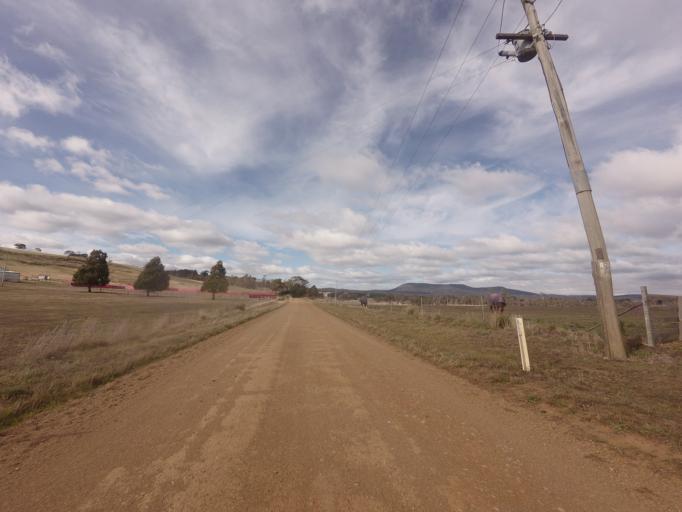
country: AU
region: Tasmania
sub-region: Sorell
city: Sorell
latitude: -42.4290
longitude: 147.4462
